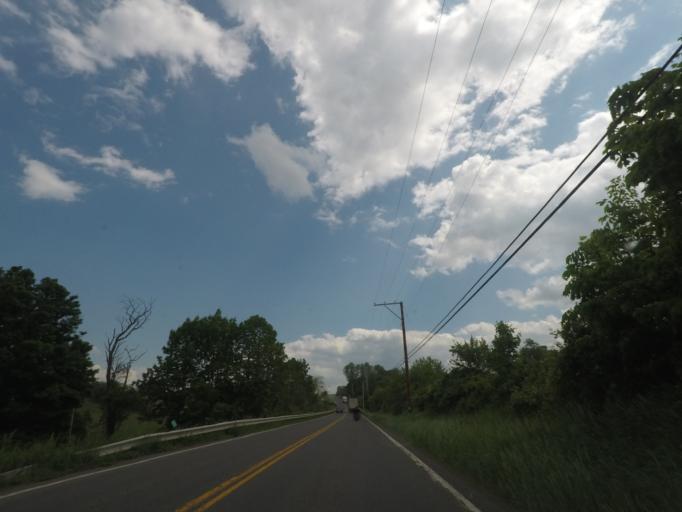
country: US
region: New York
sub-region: Dutchess County
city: Pine Plains
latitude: 42.0392
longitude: -73.6160
